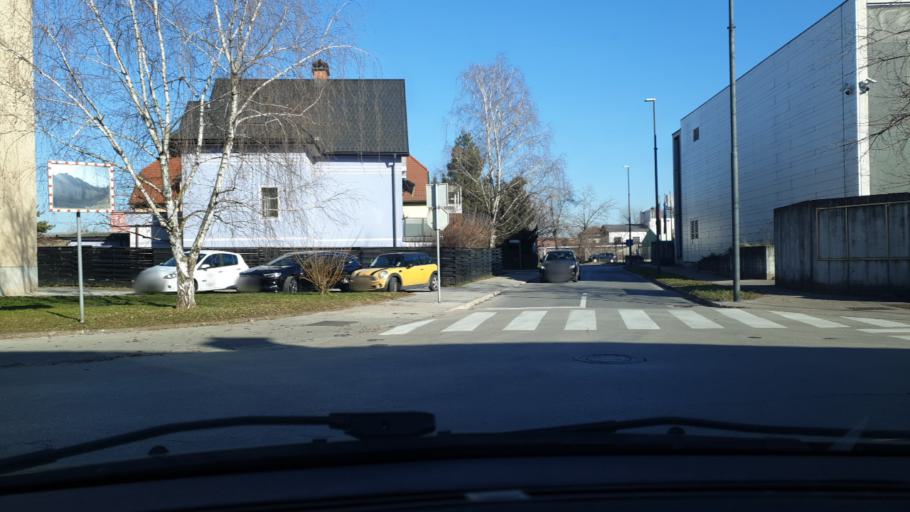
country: SI
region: Ljubljana
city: Ljubljana
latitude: 46.0611
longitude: 14.5330
